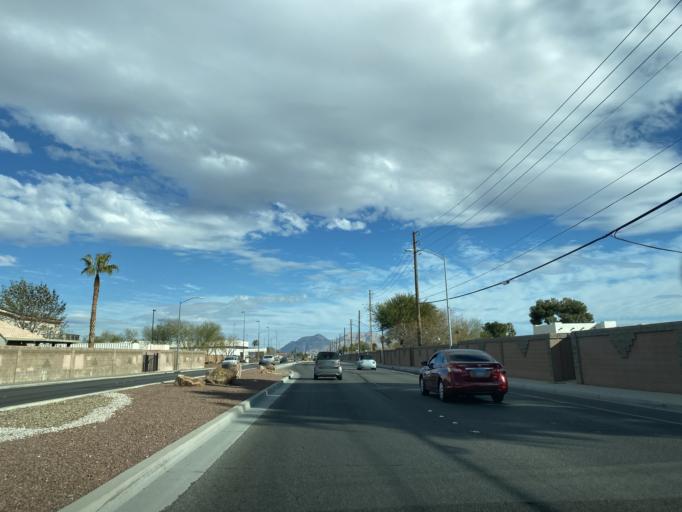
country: US
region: Nevada
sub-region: Clark County
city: Las Vegas
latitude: 36.1884
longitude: -115.1663
